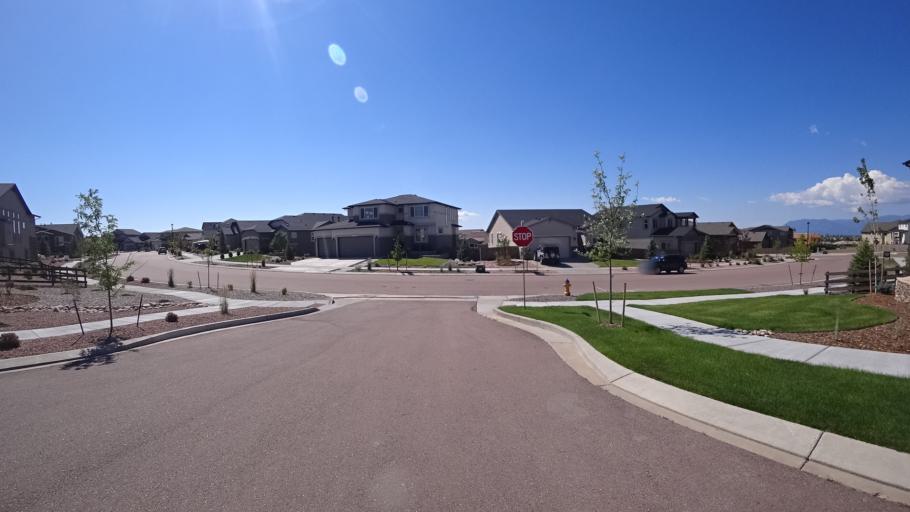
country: US
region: Colorado
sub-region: El Paso County
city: Black Forest
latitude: 38.9798
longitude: -104.7495
